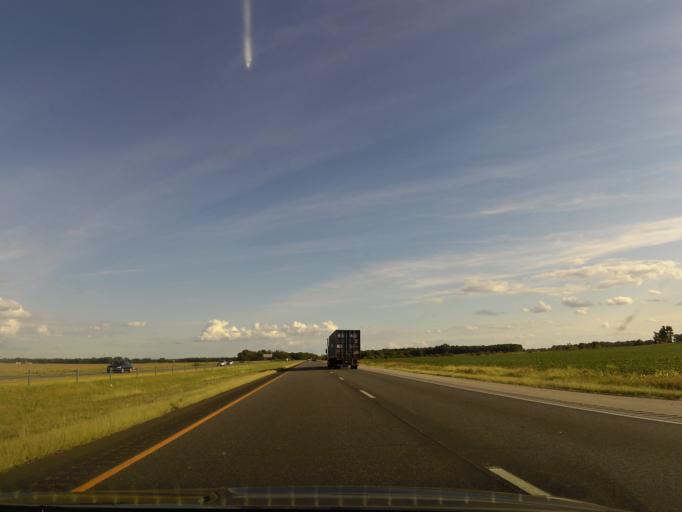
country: US
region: Indiana
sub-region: Jasper County
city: Rensselaer
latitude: 40.8547
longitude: -87.1820
